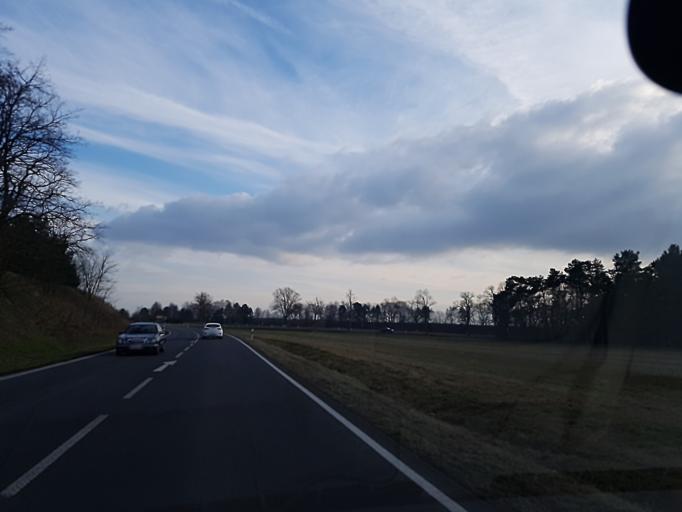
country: DE
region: Brandenburg
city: Belzig
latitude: 52.1343
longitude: 12.6241
